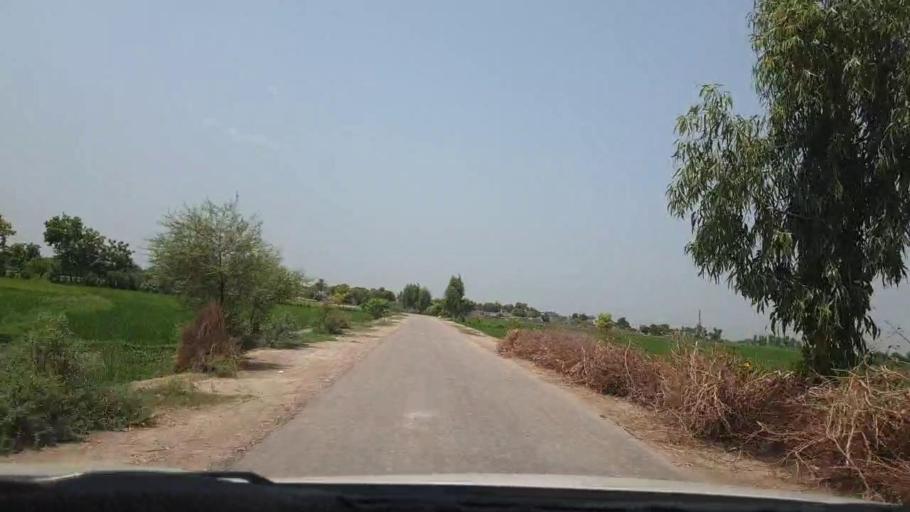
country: PK
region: Sindh
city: Radhan
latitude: 27.2405
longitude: 68.0109
